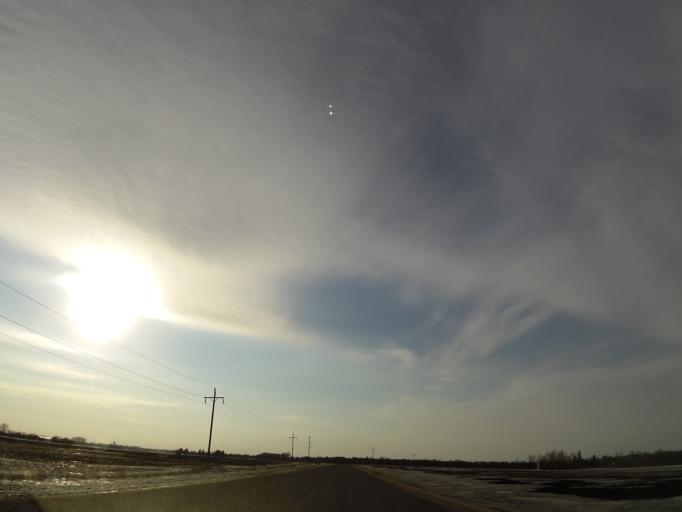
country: US
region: North Dakota
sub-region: Walsh County
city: Grafton
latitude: 48.4198
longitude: -97.3704
